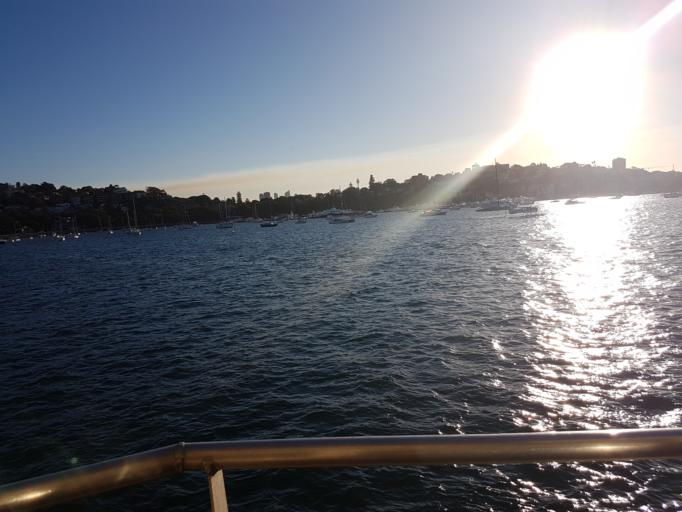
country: AU
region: New South Wales
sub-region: Woollahra
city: Point Piper
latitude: -33.8691
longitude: 151.2624
